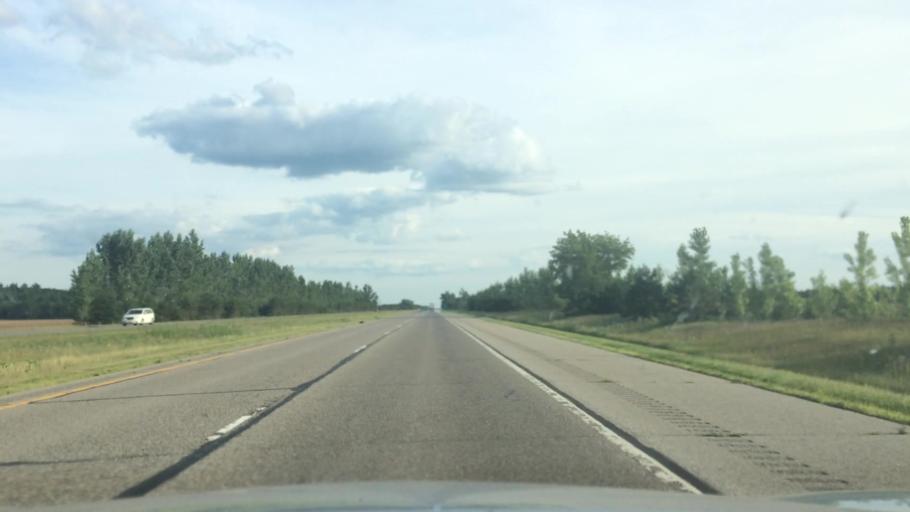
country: US
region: Wisconsin
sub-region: Portage County
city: Plover
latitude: 44.2868
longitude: -89.5237
